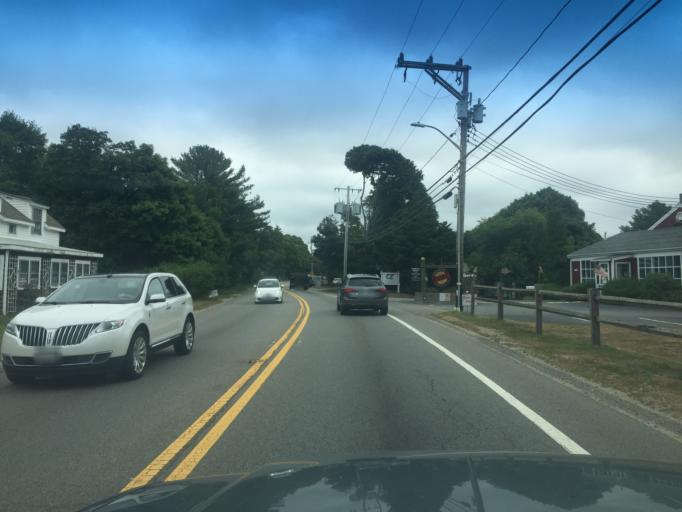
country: US
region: Massachusetts
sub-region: Barnstable County
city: Cotuit
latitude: 41.6395
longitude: -70.4456
